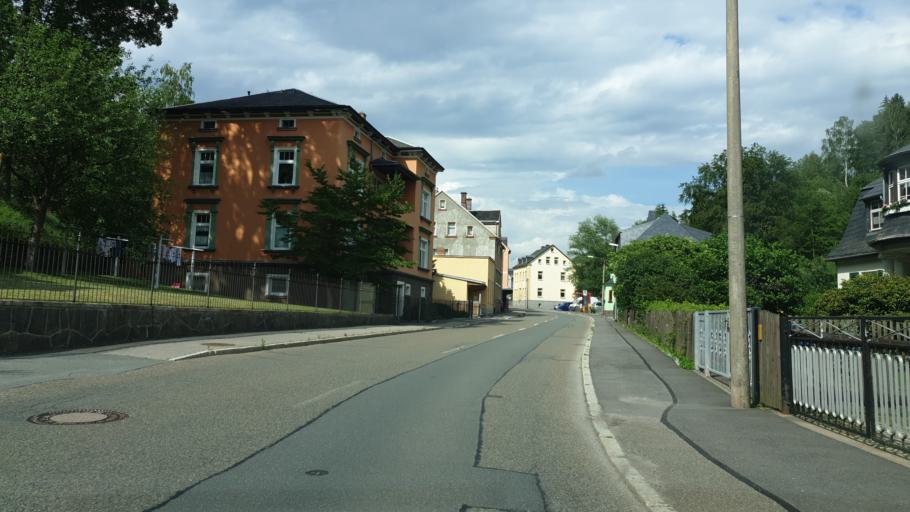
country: DE
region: Saxony
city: Aue
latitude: 50.6057
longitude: 12.7002
